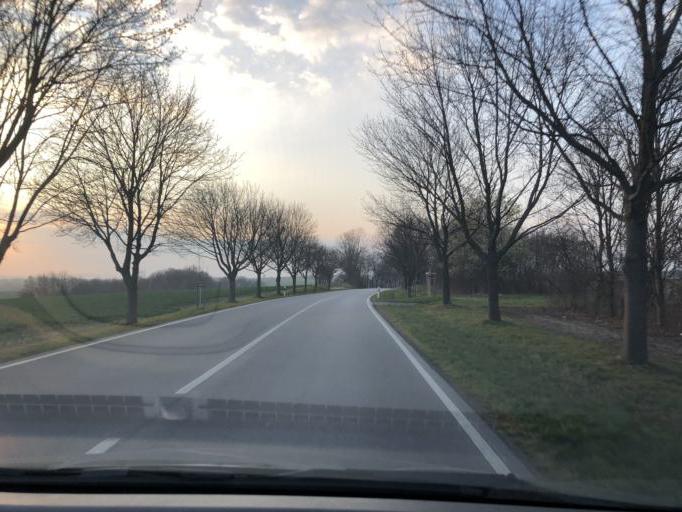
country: DE
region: Saxony
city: Goda
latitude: 51.2007
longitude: 14.3148
